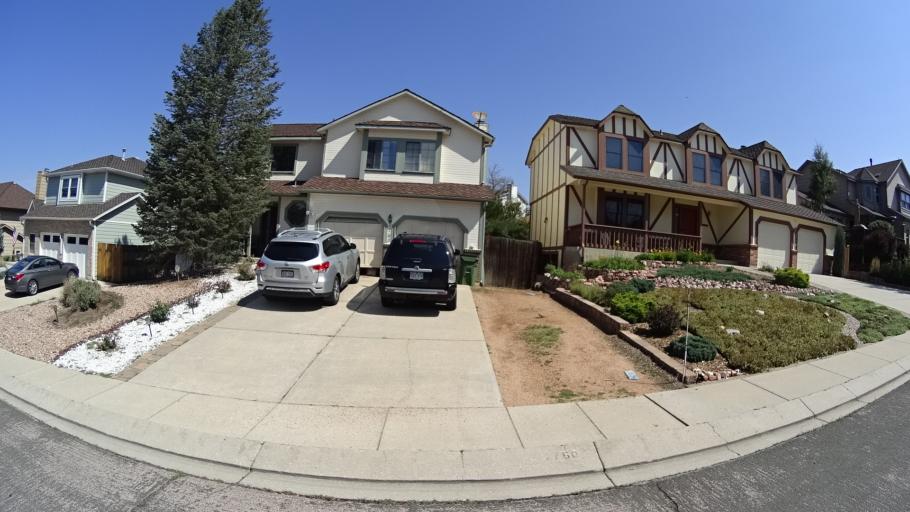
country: US
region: Colorado
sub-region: El Paso County
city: Black Forest
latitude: 38.9564
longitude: -104.7742
